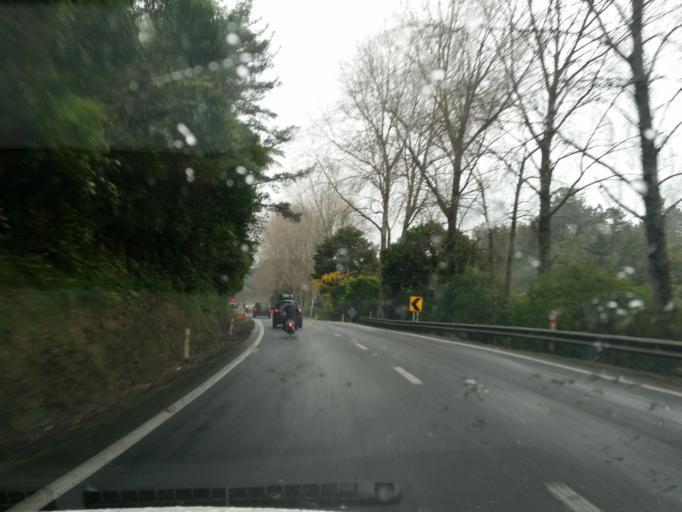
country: NZ
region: Waikato
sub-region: Hauraki District
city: Waihi
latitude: -37.4179
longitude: 175.7609
